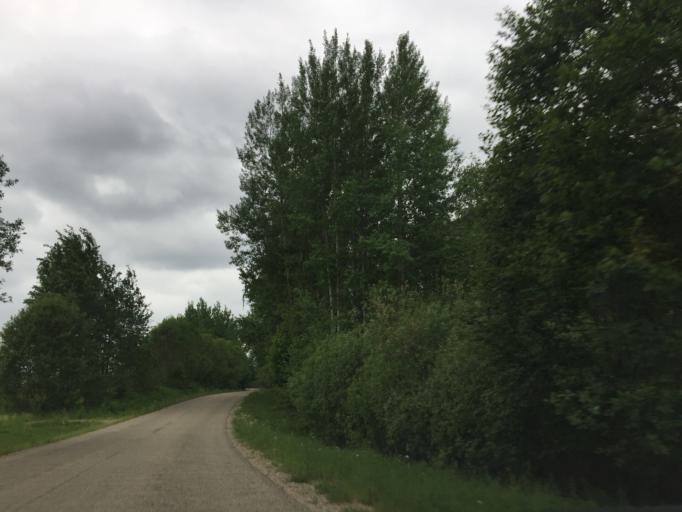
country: LV
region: Aglona
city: Aglona
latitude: 56.0784
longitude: 26.9126
